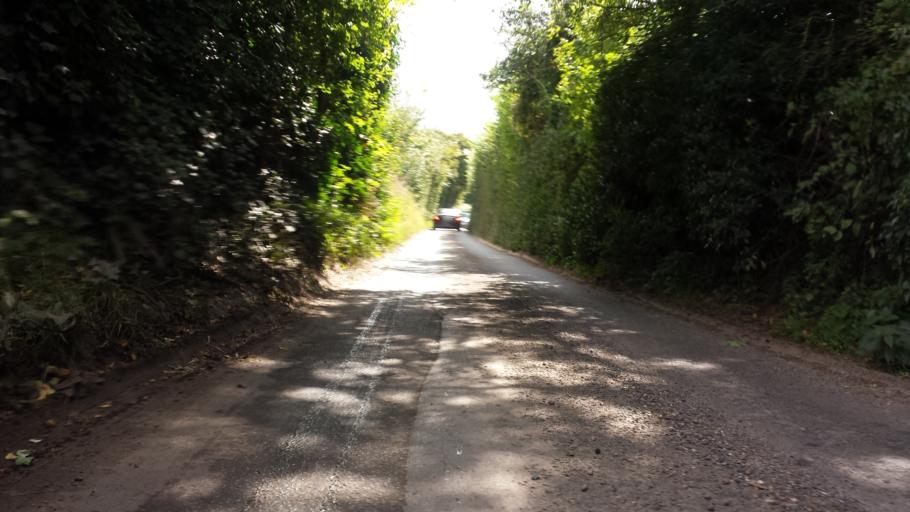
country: GB
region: England
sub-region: Kent
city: Swanley
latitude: 51.4017
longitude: 0.1939
